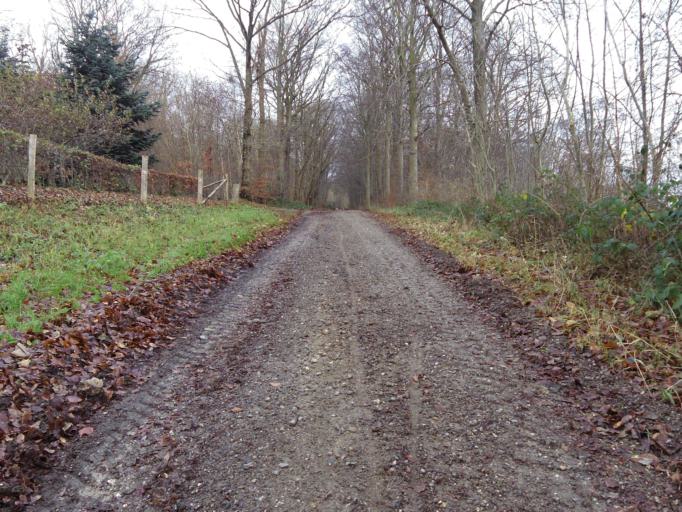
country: DK
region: South Denmark
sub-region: Aabenraa Kommune
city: Krusa
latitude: 54.9379
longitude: 9.4392
